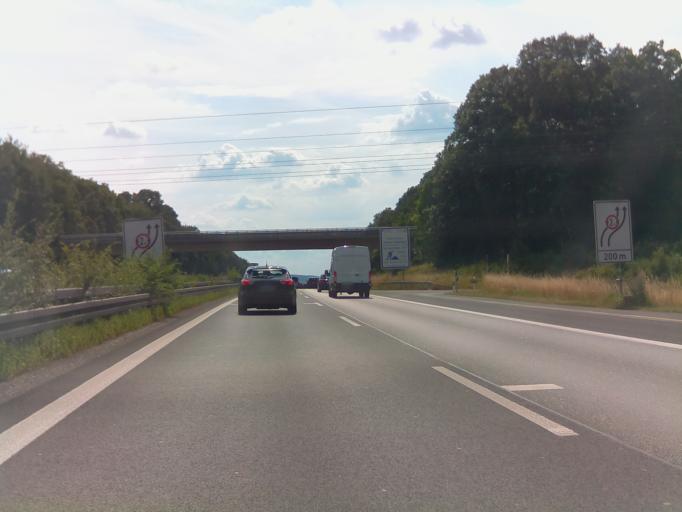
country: DE
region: Bavaria
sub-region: Regierungsbezirk Unterfranken
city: Werneck
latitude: 49.9902
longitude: 10.0666
